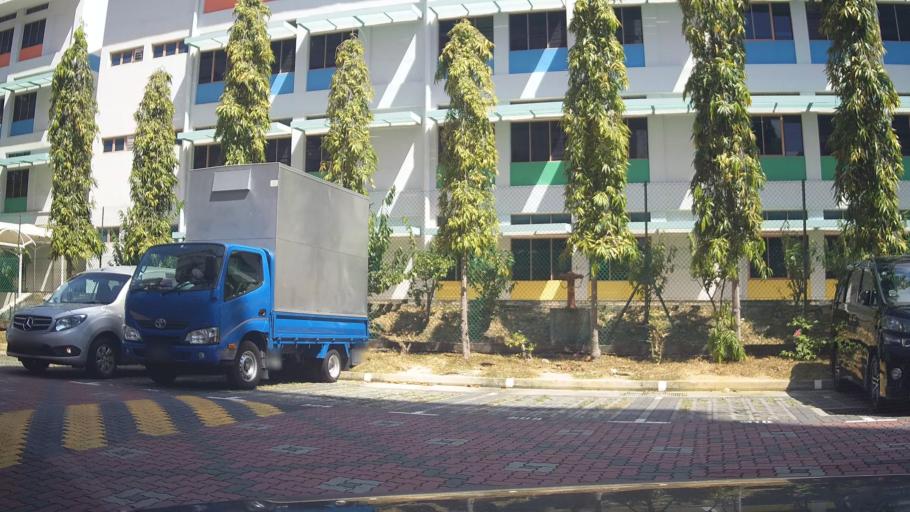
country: MY
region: Johor
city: Kampung Pasir Gudang Baru
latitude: 1.3705
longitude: 103.9567
